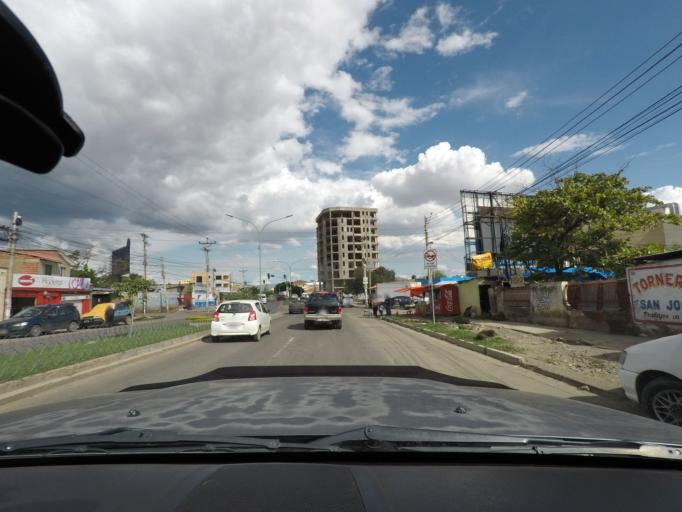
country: BO
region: Cochabamba
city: Cochabamba
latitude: -17.3734
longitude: -66.1831
